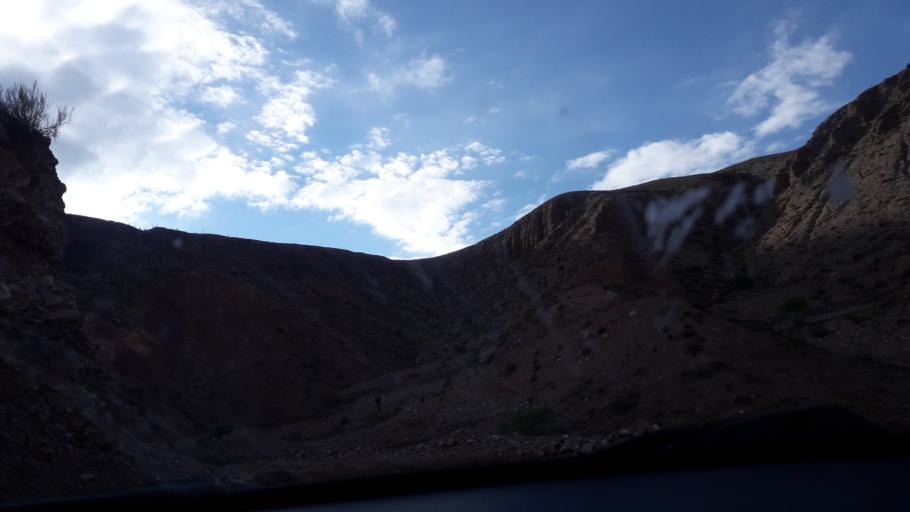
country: AR
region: Jujuy
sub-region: Departamento de Tilcara
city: Tilcara
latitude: -23.5818
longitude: -65.3856
